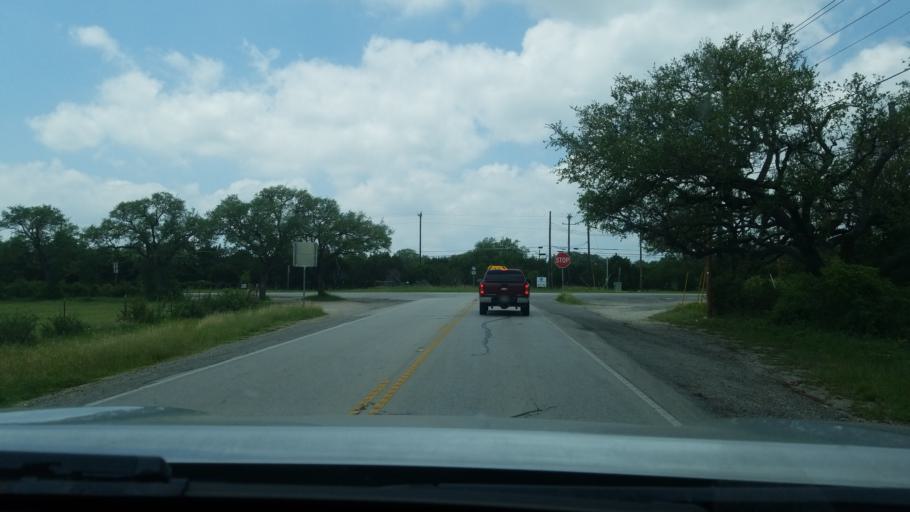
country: US
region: Texas
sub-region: Hays County
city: Dripping Springs
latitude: 30.1318
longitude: -98.0311
